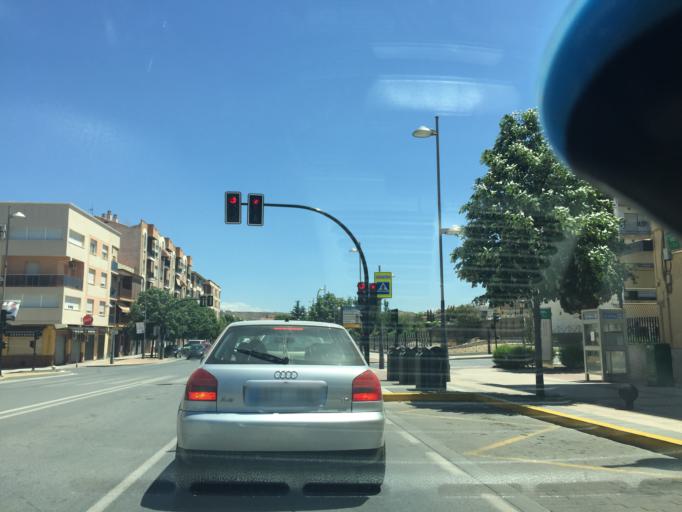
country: ES
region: Andalusia
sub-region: Provincia de Granada
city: Guadix
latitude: 37.3031
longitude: -3.1390
